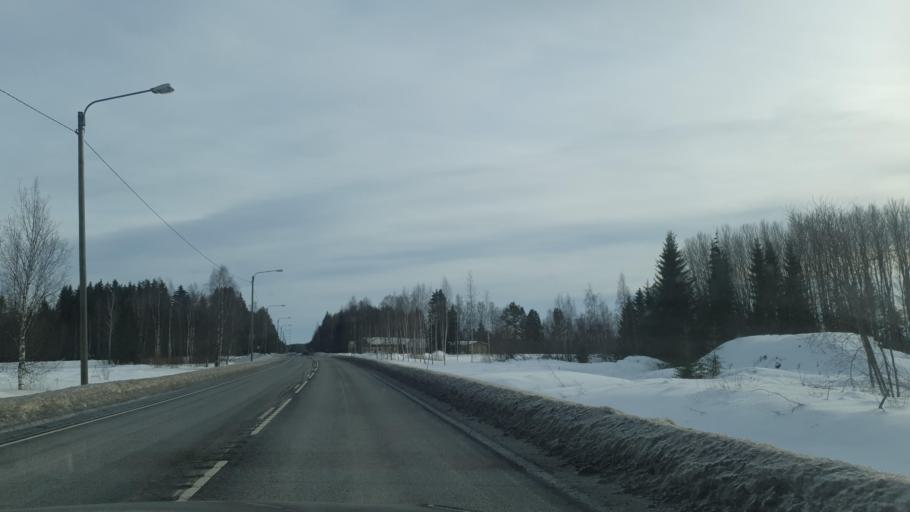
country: FI
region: Northern Ostrobothnia
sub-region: Oulu
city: Kempele
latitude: 64.9459
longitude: 25.6830
